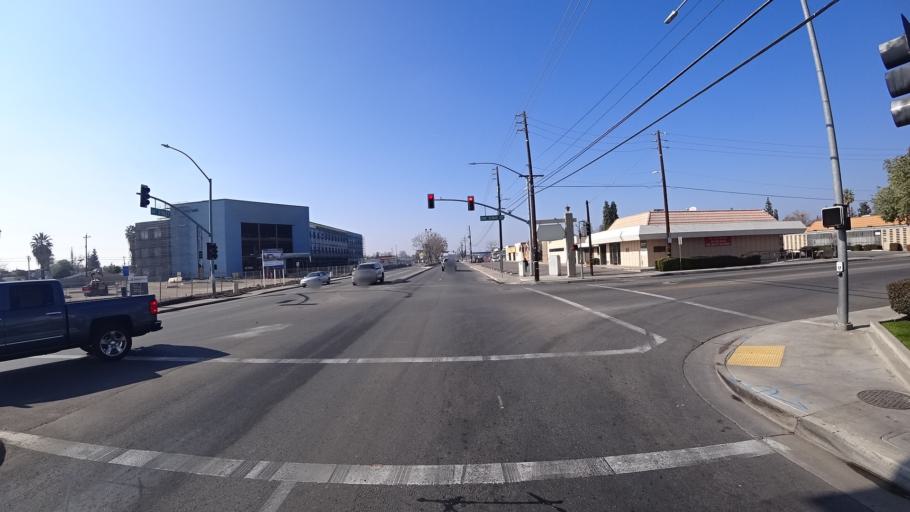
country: US
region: California
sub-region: Kern County
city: Bakersfield
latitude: 35.3905
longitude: -119.0081
